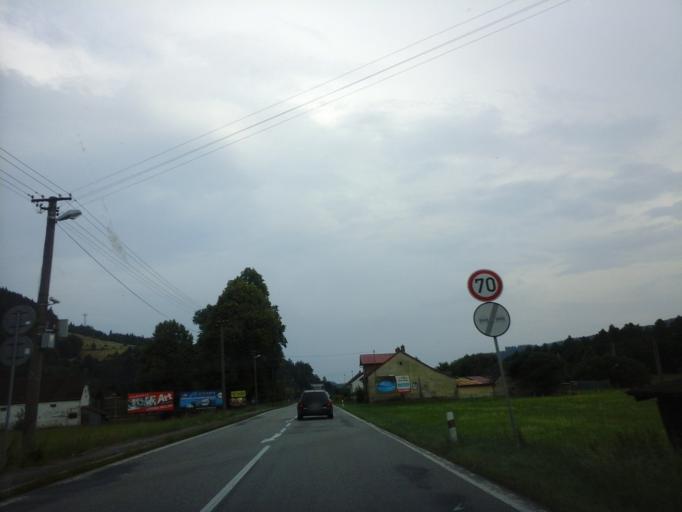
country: CZ
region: Pardubicky
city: Brnenec
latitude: 49.5993
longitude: 16.5349
